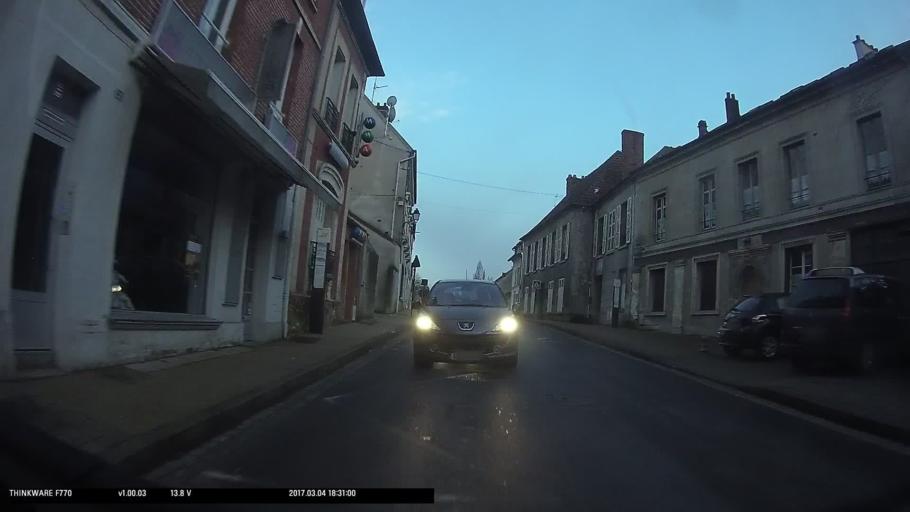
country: FR
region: Ile-de-France
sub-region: Departement du Val-d'Oise
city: Marines
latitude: 49.1431
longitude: 1.9806
